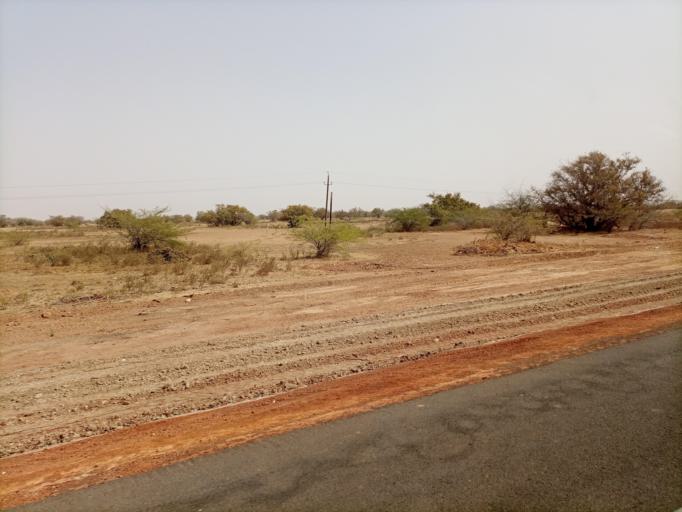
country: SN
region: Fatick
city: Foundiougne
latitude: 14.1622
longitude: -16.4662
